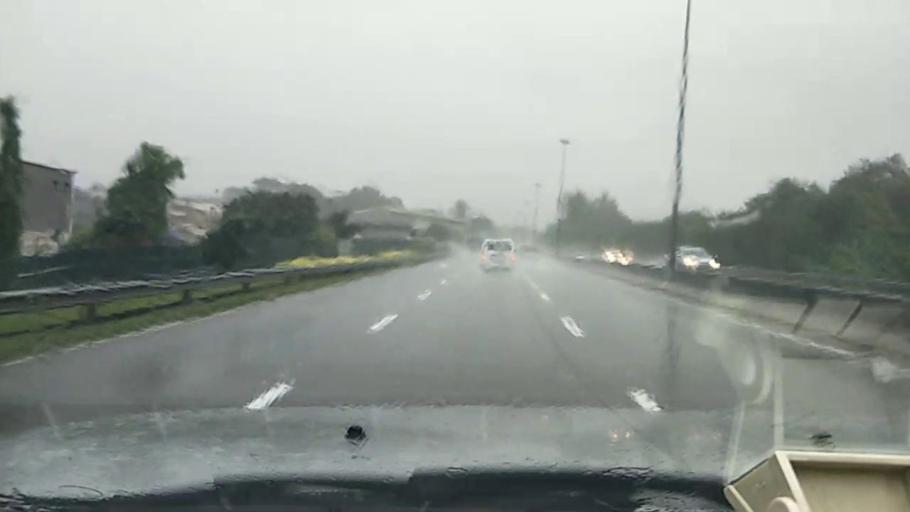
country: MY
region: Selangor
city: Kampong Baharu Balakong
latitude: 3.0015
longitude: 101.7742
